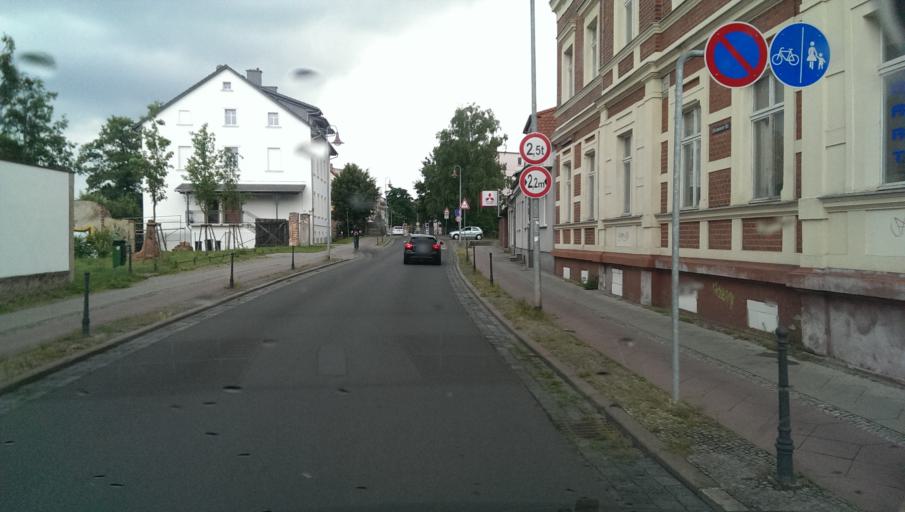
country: DE
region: Brandenburg
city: Rathenow
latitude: 52.6111
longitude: 12.3337
